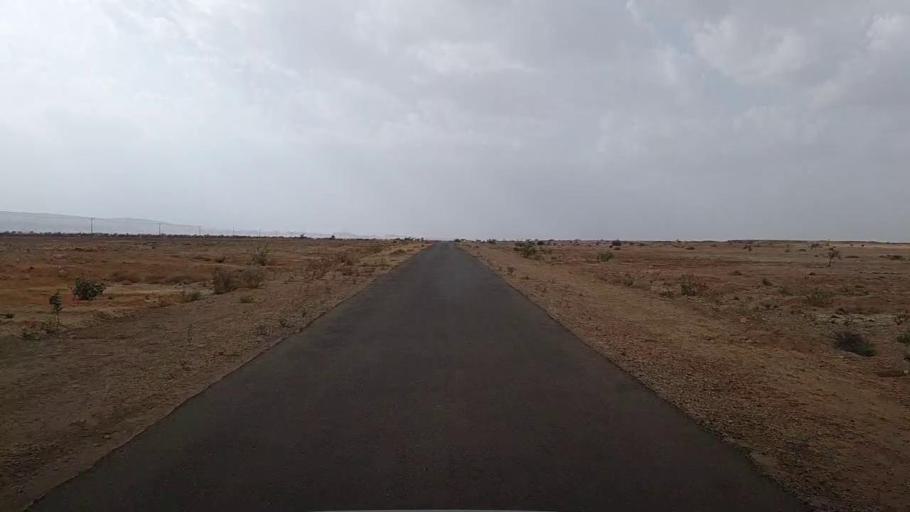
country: PK
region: Sindh
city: Jamshoro
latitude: 25.4338
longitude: 67.6865
